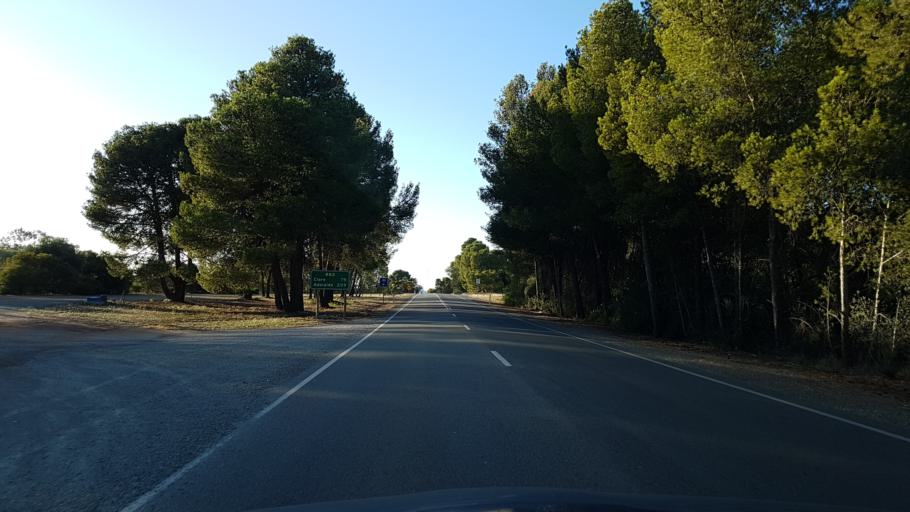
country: AU
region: South Australia
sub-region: Port Pirie City and Dists
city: Crystal Brook
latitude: -33.2682
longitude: 138.3495
